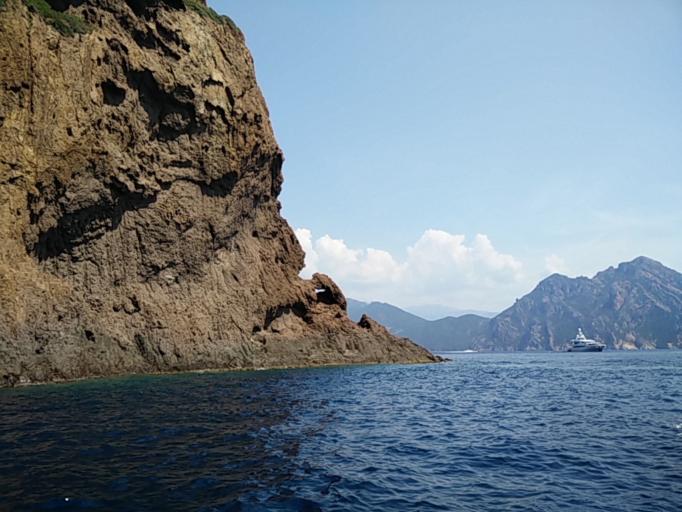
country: FR
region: Corsica
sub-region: Departement de la Corse-du-Sud
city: Cargese
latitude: 42.3356
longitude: 8.5663
